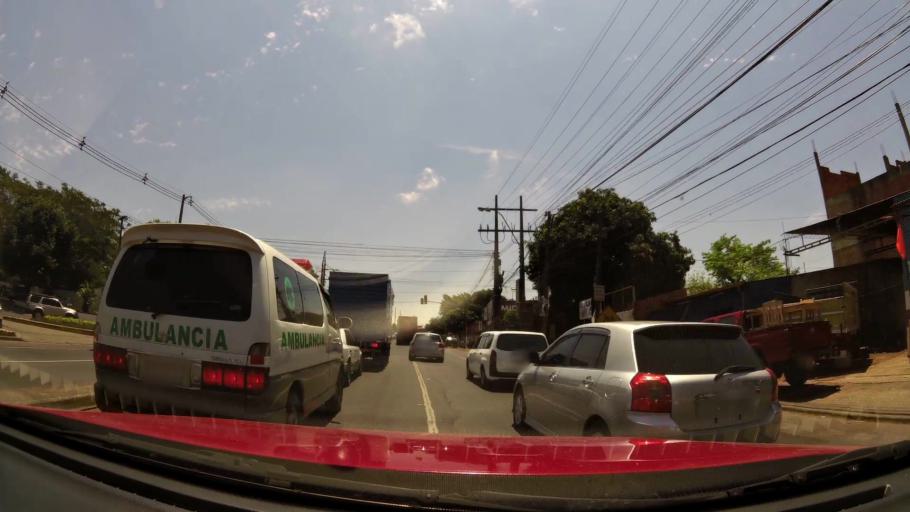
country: PY
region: Central
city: Villa Elisa
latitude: -25.3562
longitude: -57.5699
